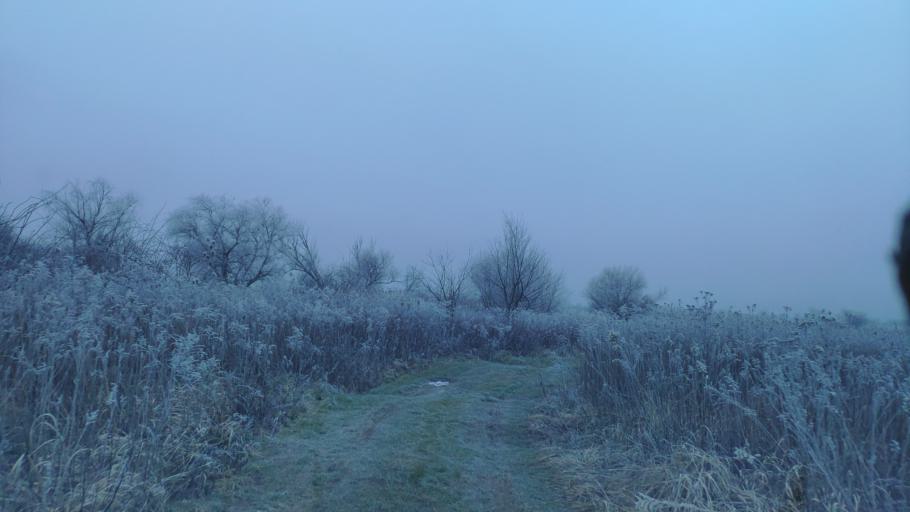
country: SK
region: Kosicky
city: Kosice
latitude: 48.6178
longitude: 21.3315
